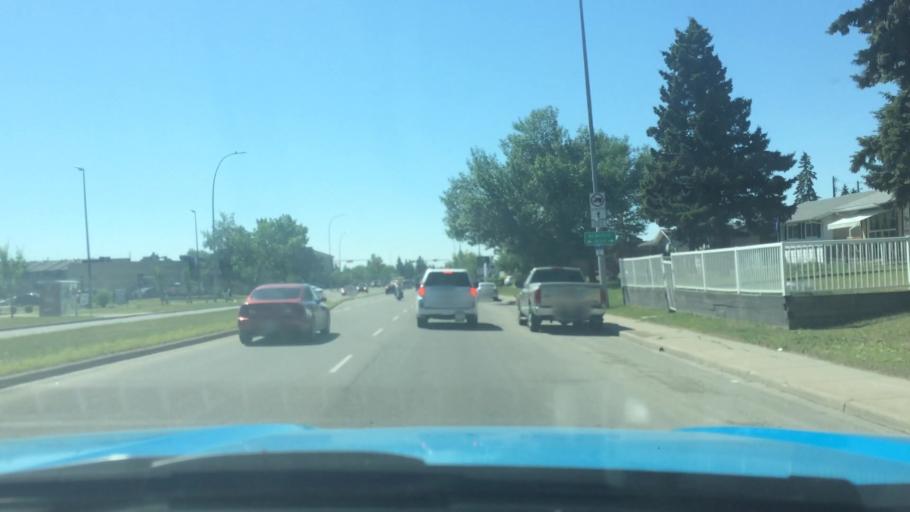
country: CA
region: Alberta
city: Calgary
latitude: 51.0549
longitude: -113.9566
